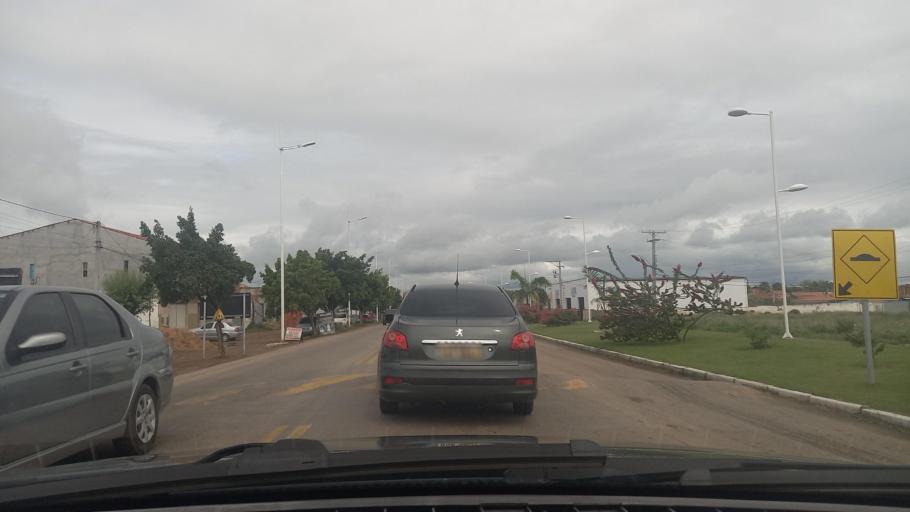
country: BR
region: Bahia
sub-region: Paulo Afonso
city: Paulo Afonso
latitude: -9.4415
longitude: -38.2237
